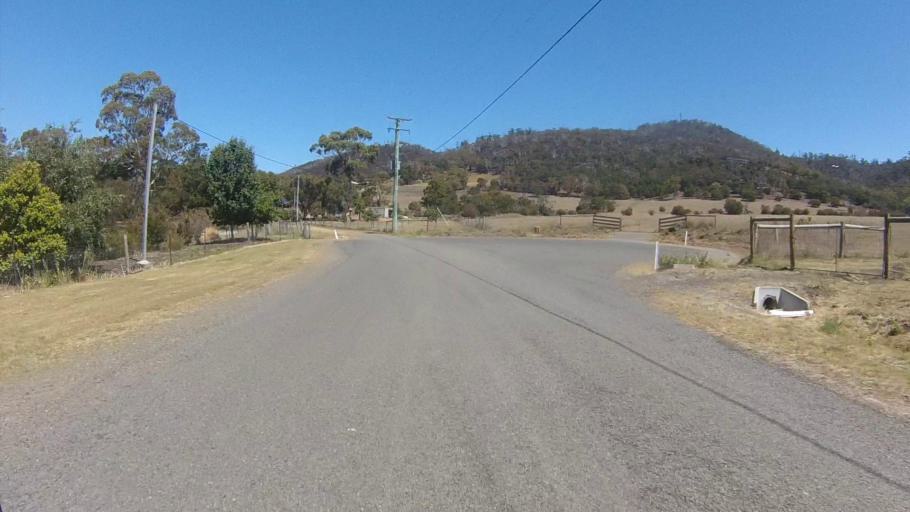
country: AU
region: Tasmania
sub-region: Clarence
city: Cambridge
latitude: -42.8494
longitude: 147.4632
